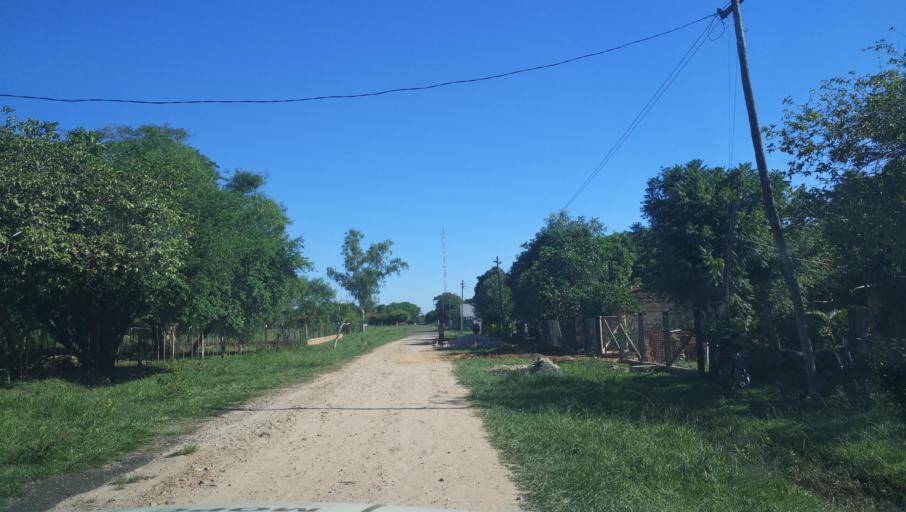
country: PY
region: Caaguazu
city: Carayao
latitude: -25.2019
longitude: -56.3999
